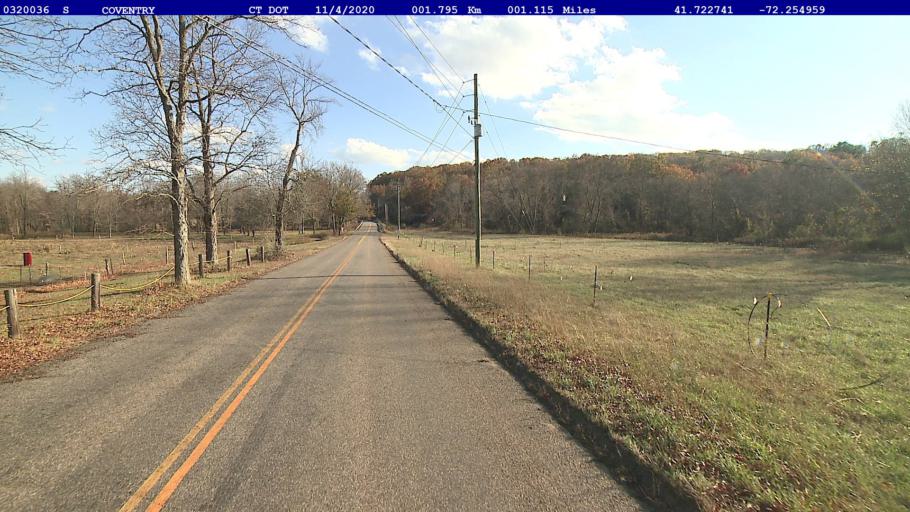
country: US
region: Connecticut
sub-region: Tolland County
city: Mansfield City
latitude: 41.7227
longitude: -72.2550
